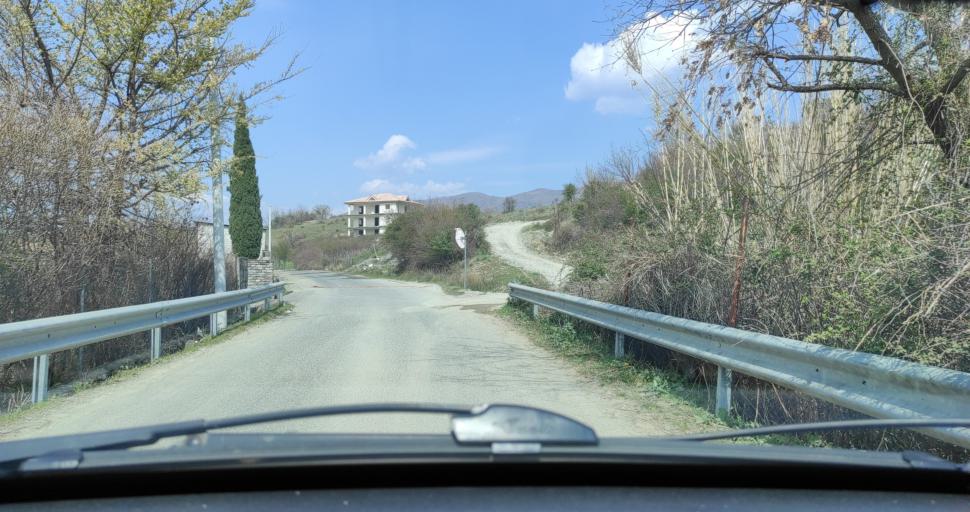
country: AL
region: Lezhe
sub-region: Rrethi i Lezhes
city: Kallmeti i Madh
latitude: 41.8608
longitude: 19.6991
